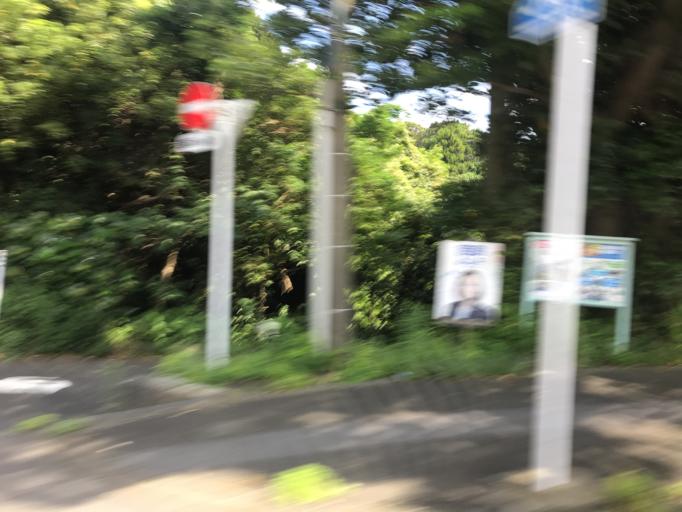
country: JP
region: Shizuoka
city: Ito
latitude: 34.7839
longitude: 139.3893
